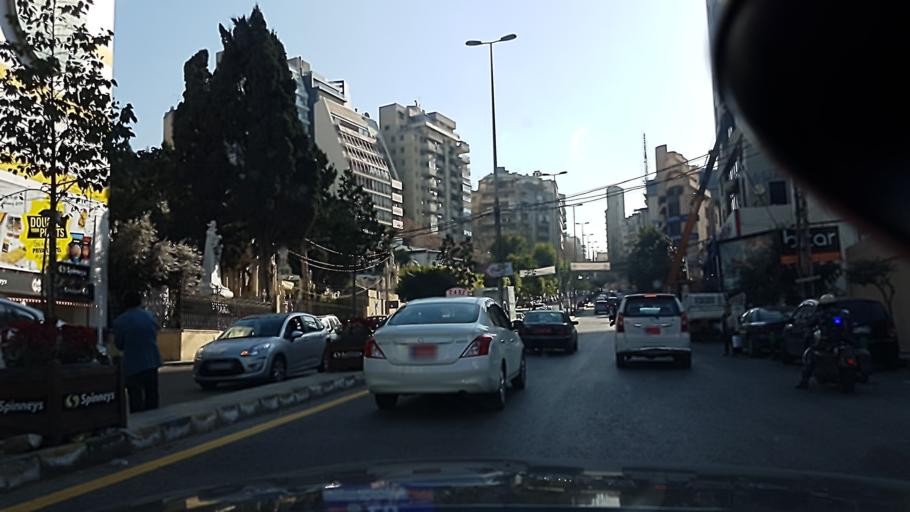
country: LB
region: Beyrouth
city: Beirut
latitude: 33.8911
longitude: 35.5208
